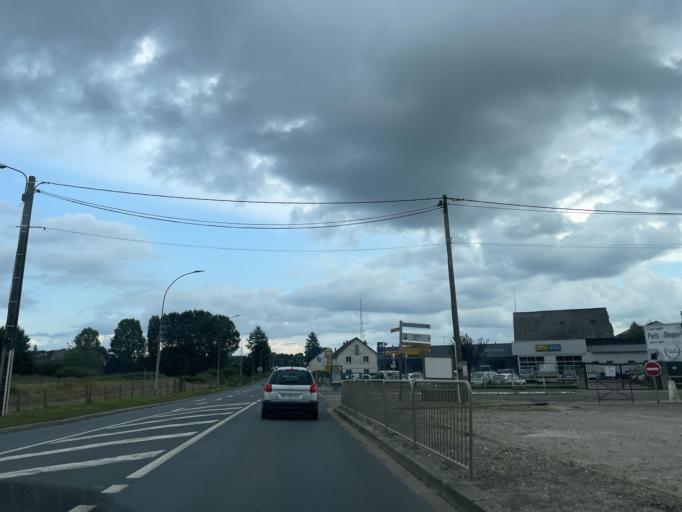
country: FR
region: Haute-Normandie
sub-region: Departement de la Seine-Maritime
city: Gournay-en-Bray
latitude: 49.4857
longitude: 1.7227
